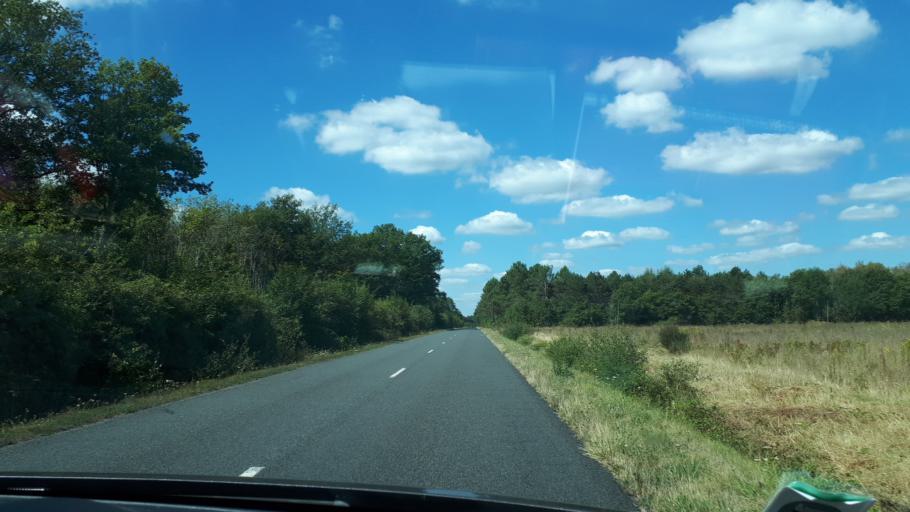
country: FR
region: Centre
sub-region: Departement du Loir-et-Cher
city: Dhuizon
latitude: 47.5345
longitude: 1.7023
